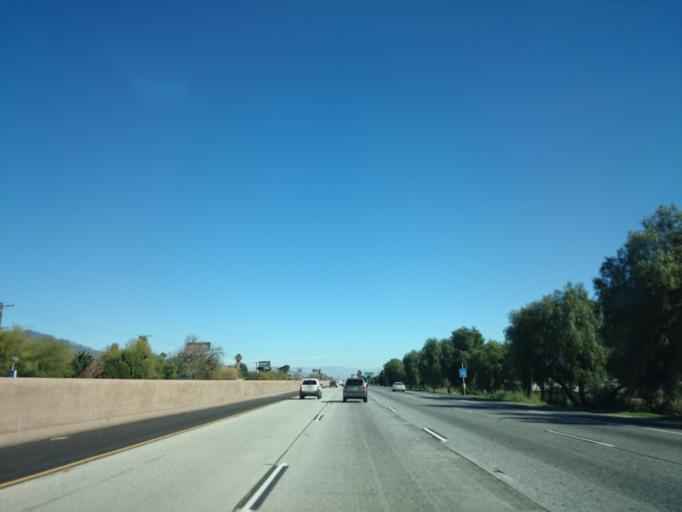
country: US
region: California
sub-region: Riverside County
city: Banning
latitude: 33.9241
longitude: -116.8926
